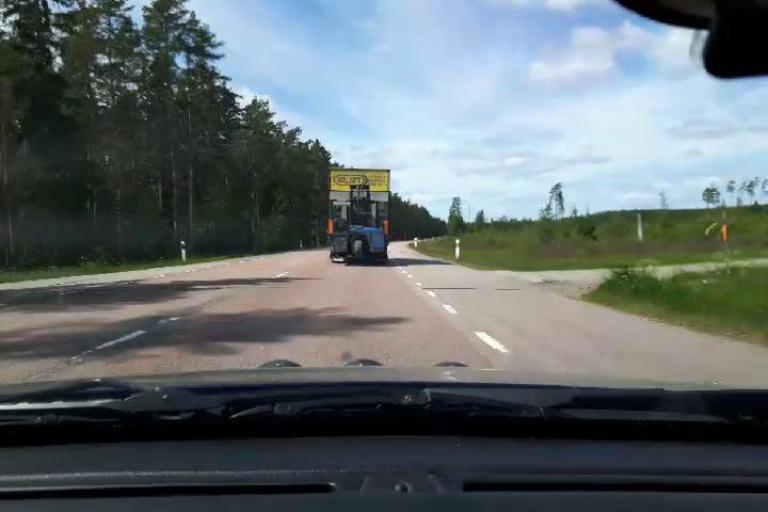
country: SE
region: Uppsala
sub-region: Osthammars Kommun
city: Bjorklinge
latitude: 60.1132
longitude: 17.5245
